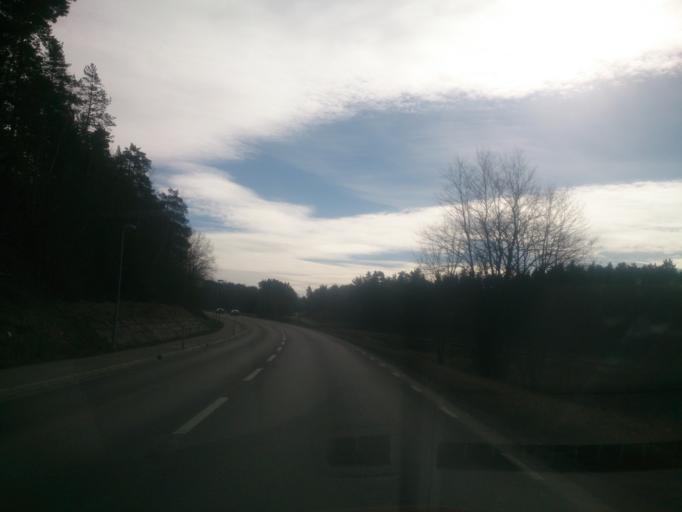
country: SE
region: OEstergoetland
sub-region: Norrkopings Kommun
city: Kimstad
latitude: 58.5535
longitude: 15.9562
